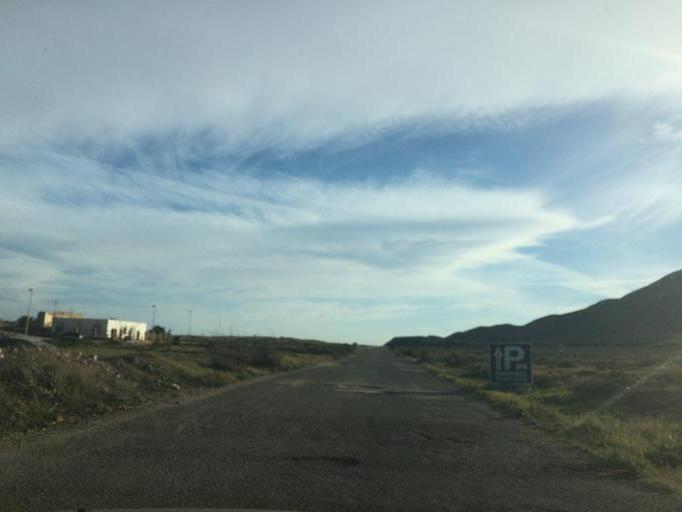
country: ES
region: Andalusia
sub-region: Provincia de Almeria
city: San Jose
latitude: 36.8029
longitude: -2.0641
